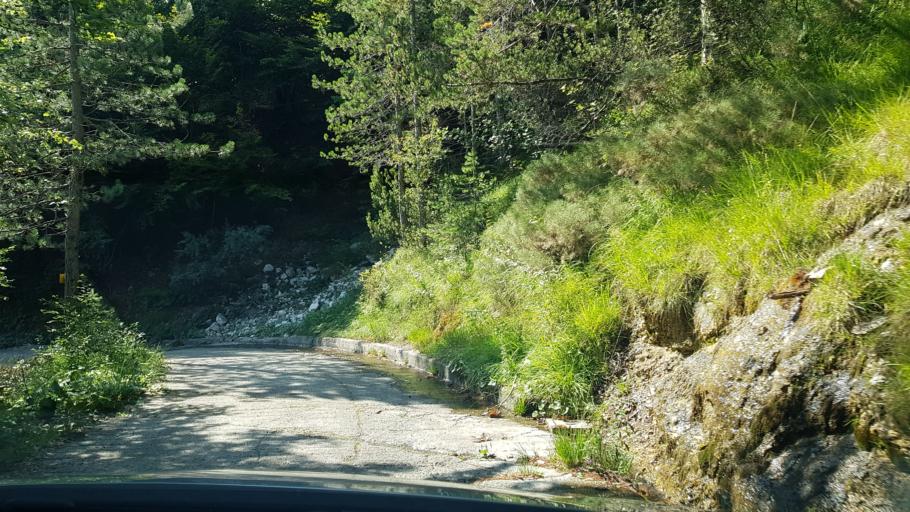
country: IT
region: Friuli Venezia Giulia
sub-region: Provincia di Udine
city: Moggio Udinese
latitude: 46.4470
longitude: 13.2156
